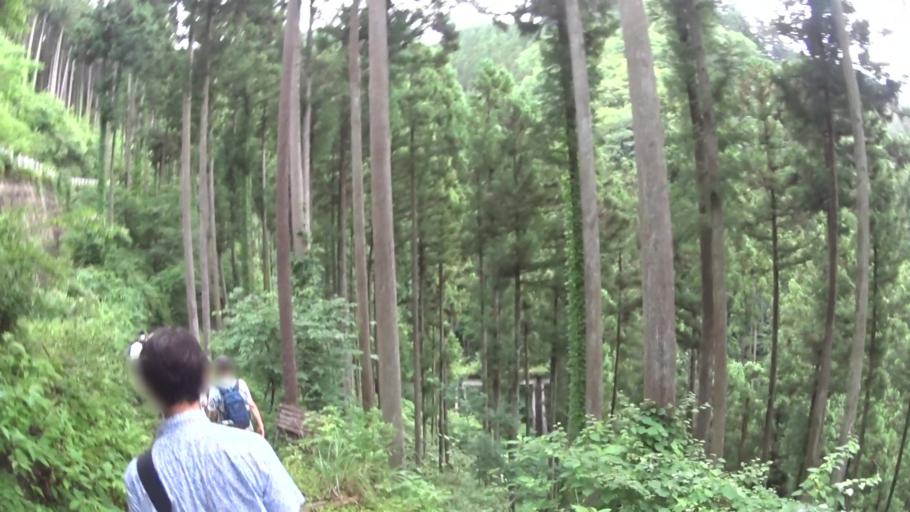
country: JP
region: Tokyo
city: Itsukaichi
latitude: 35.8036
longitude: 139.0904
